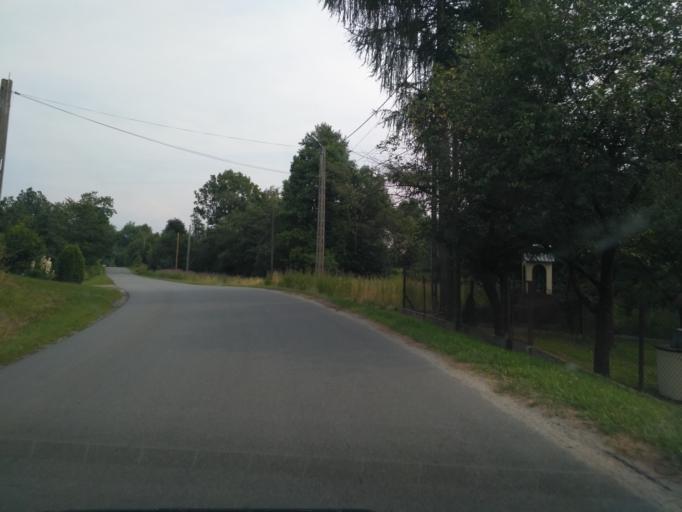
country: PL
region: Subcarpathian Voivodeship
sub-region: Powiat strzyzowski
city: Gwoznica Gorna
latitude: 49.8399
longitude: 21.9832
